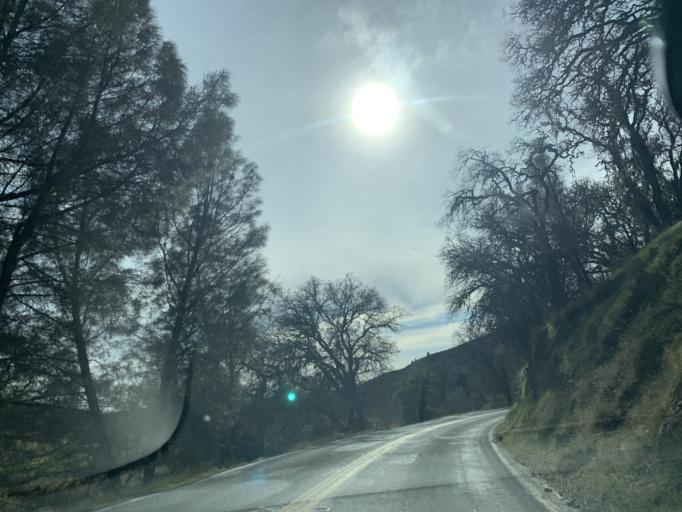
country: US
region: California
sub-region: Monterey County
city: Soledad
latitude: 36.5294
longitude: -121.1443
